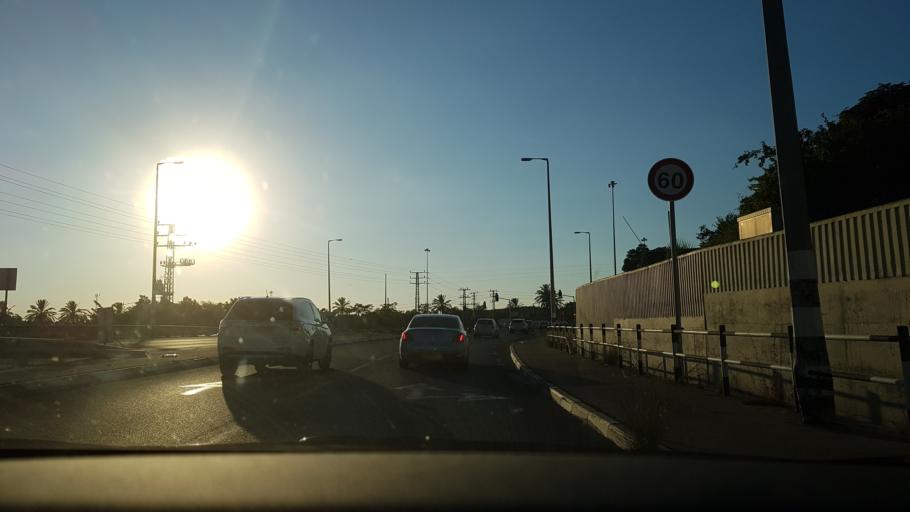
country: IL
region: Central District
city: Ness Ziona
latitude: 31.9202
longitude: 34.7732
